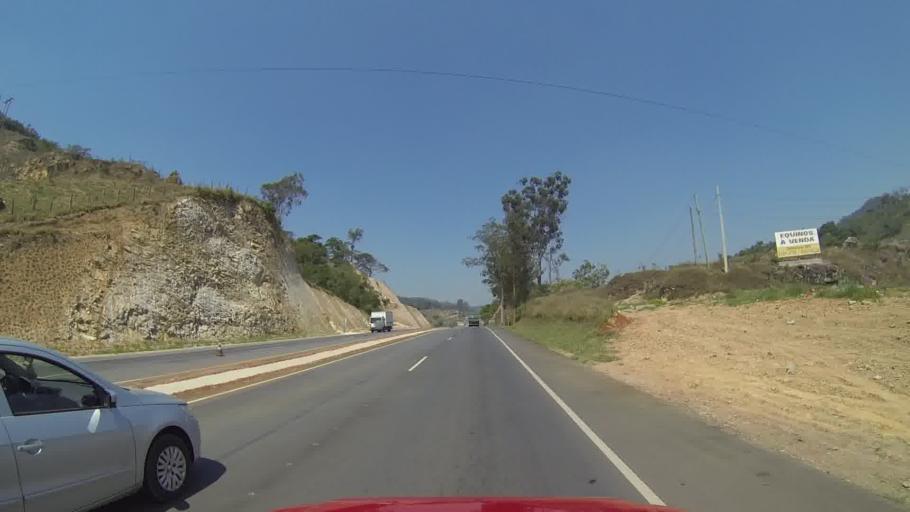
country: BR
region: Minas Gerais
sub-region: Mateus Leme
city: Mateus Leme
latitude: -20.0158
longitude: -44.4896
